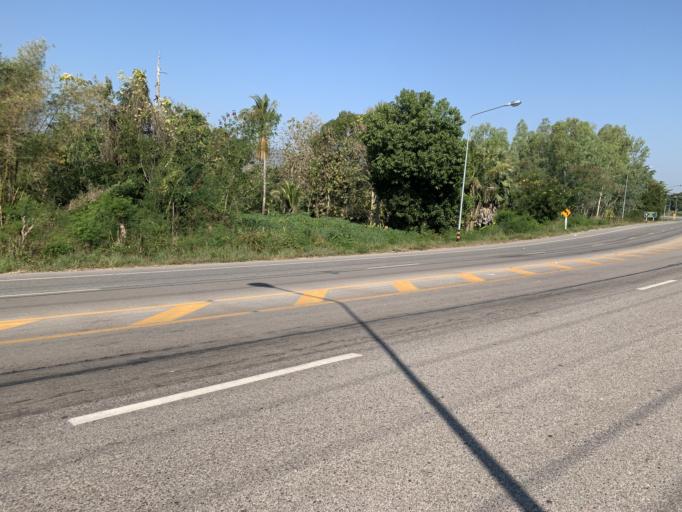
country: TH
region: Uttaradit
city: Thong Saen Khan
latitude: 17.2381
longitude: 100.3370
